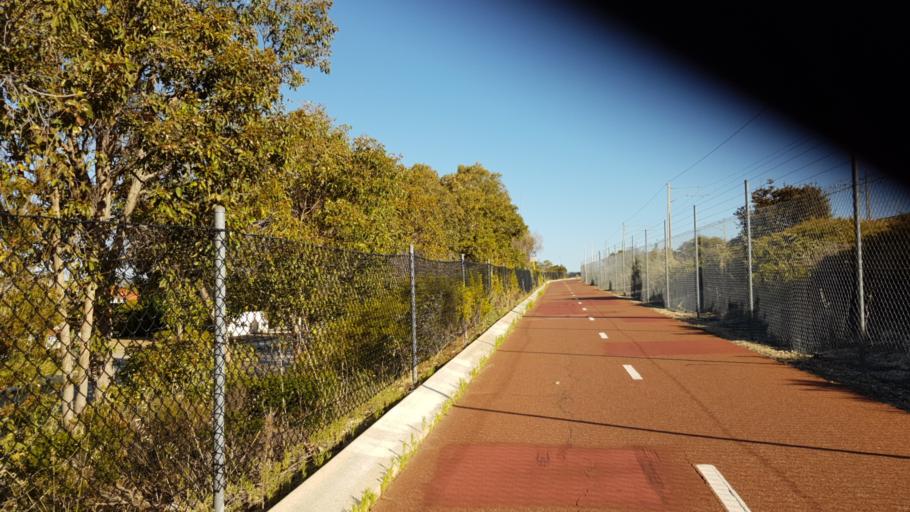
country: AU
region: Western Australia
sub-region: Gosnells
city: Kenwick
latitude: -32.0309
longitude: 115.9638
